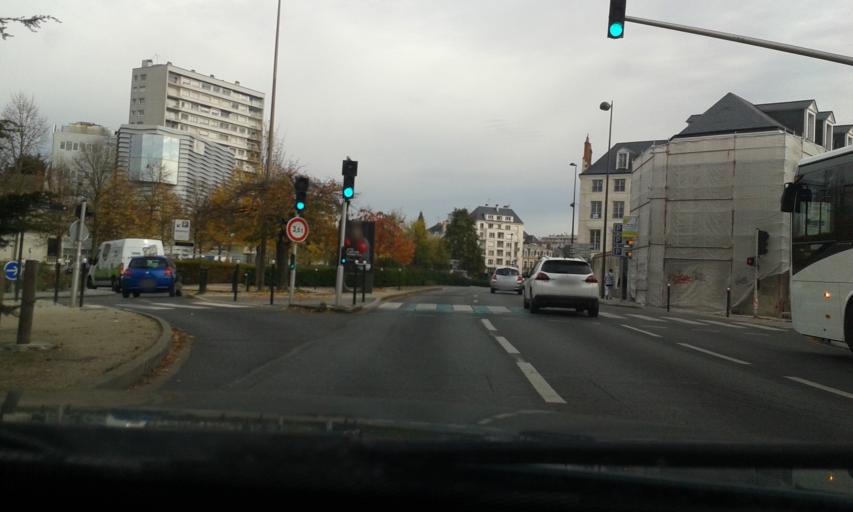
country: FR
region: Centre
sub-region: Departement du Loiret
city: Orleans
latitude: 47.9060
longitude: 1.8994
